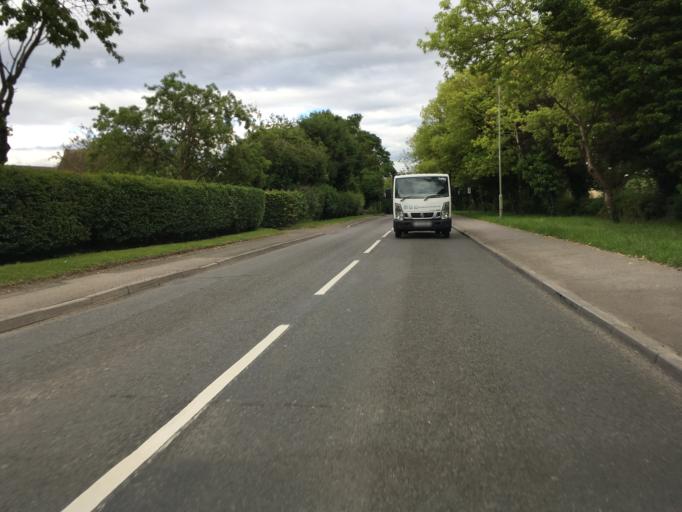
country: GB
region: England
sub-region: Oxfordshire
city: Boars Hill
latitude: 51.7062
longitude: -1.3141
